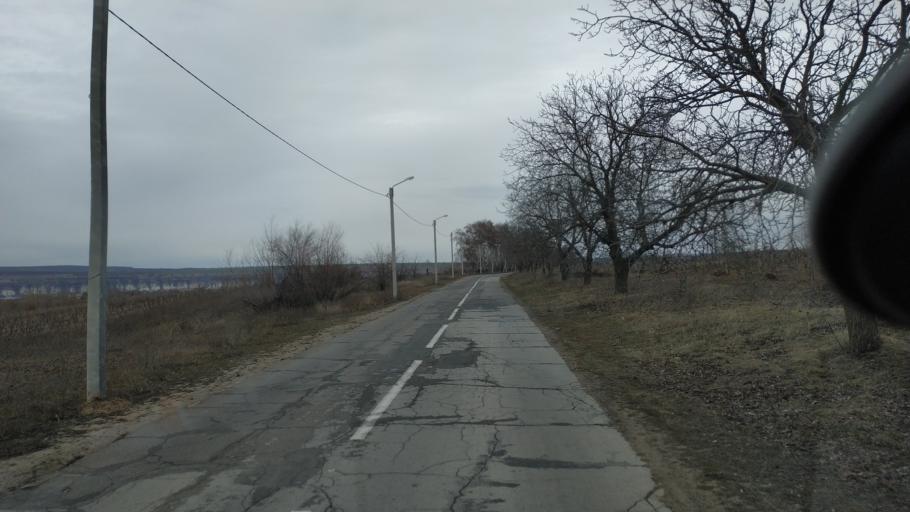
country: MD
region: Telenesti
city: Cocieri
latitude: 47.3314
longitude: 29.0969
